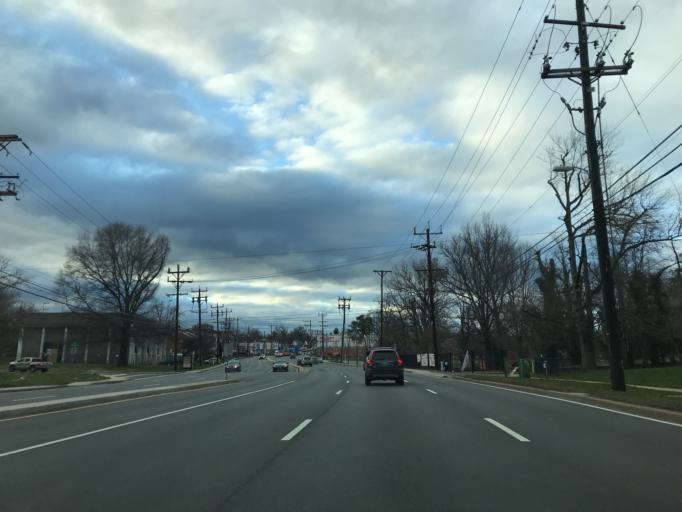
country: US
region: Maryland
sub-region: Prince George's County
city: Langley Park
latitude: 38.9968
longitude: -76.9934
